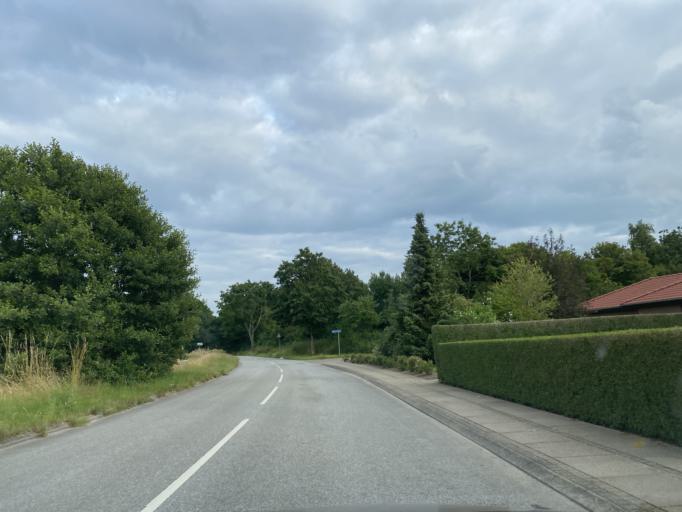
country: DK
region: Central Jutland
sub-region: Favrskov Kommune
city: Hammel
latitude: 56.2222
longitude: 9.7474
